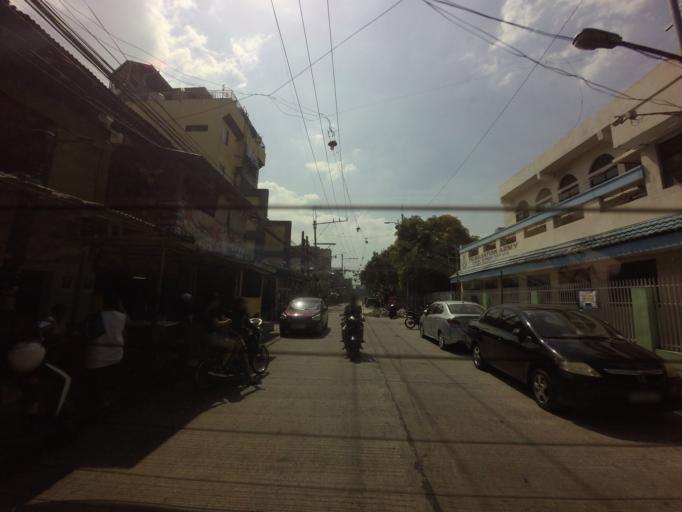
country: PH
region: Metro Manila
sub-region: City of Manila
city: Manila
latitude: 14.6181
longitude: 120.9659
